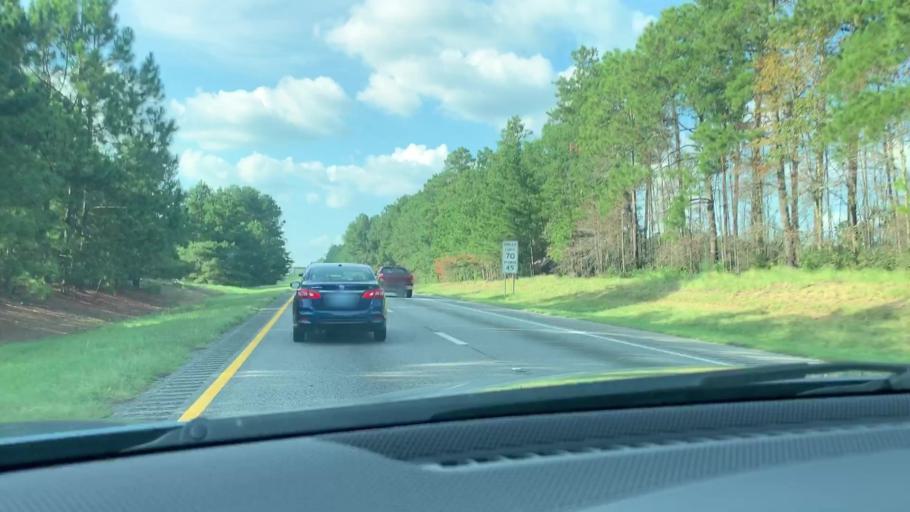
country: US
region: South Carolina
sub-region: Calhoun County
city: Saint Matthews
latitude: 33.6449
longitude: -80.8806
